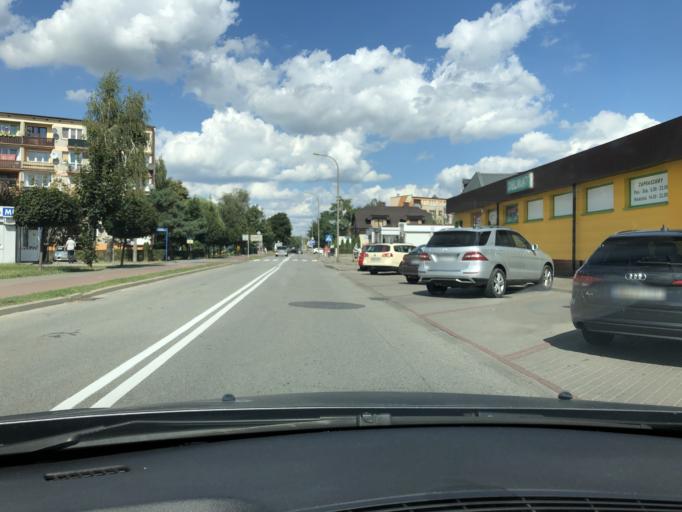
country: PL
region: Lodz Voivodeship
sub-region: Powiat wieruszowski
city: Wieruszow
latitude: 51.2965
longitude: 18.1615
